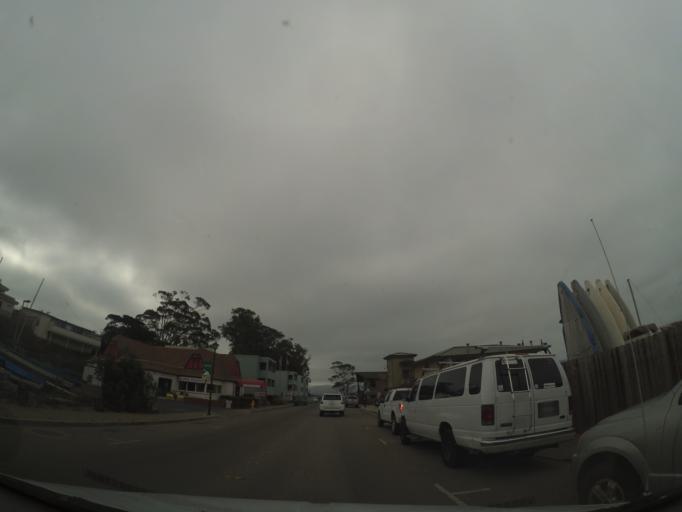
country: US
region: California
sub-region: San Luis Obispo County
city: Morro Bay
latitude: 35.3627
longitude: -120.8524
